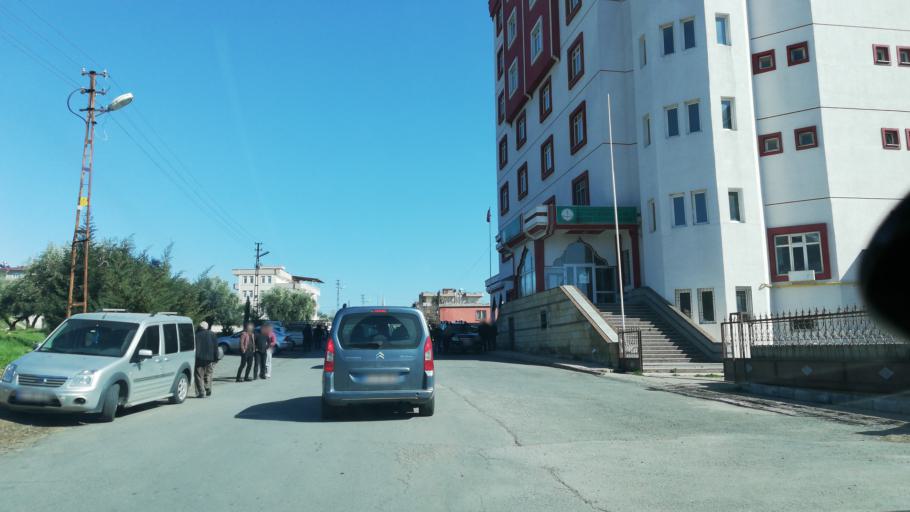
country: TR
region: Kahramanmaras
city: Kahramanmaras
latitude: 37.5750
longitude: 36.9408
